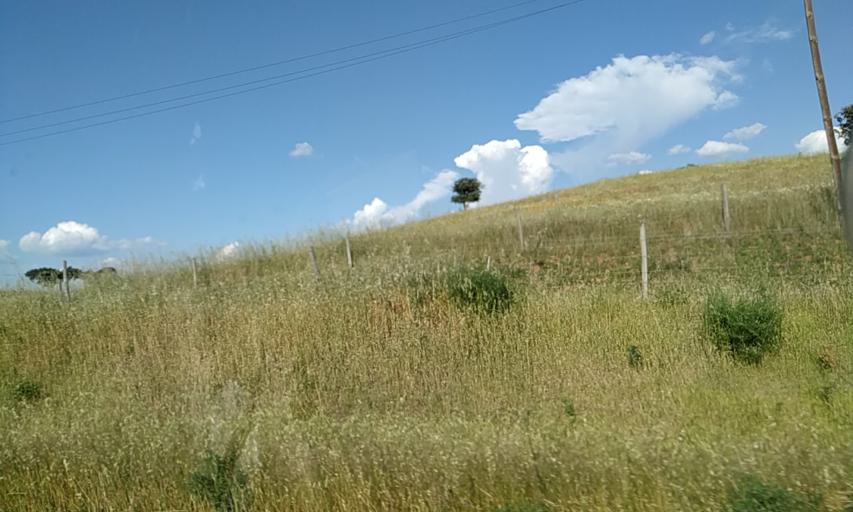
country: PT
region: Portalegre
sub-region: Fronteira
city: Fronteira
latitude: 39.0101
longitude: -7.4676
